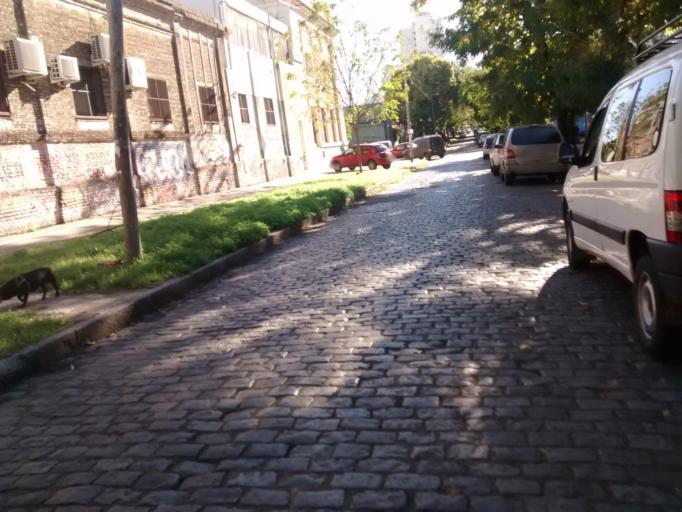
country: AR
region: Buenos Aires
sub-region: Partido de La Plata
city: La Plata
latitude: -34.9258
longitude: -57.9408
